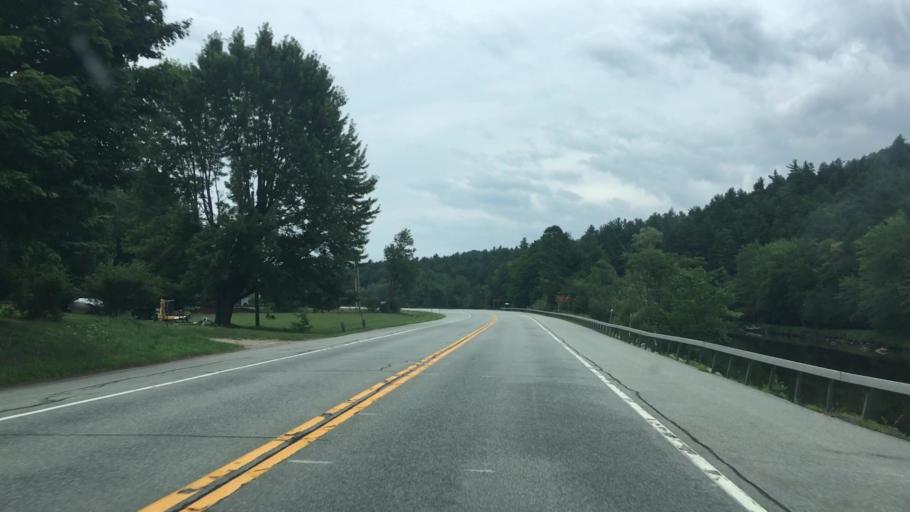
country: US
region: New York
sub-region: Essex County
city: Elizabethtown
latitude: 44.3466
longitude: -73.7618
